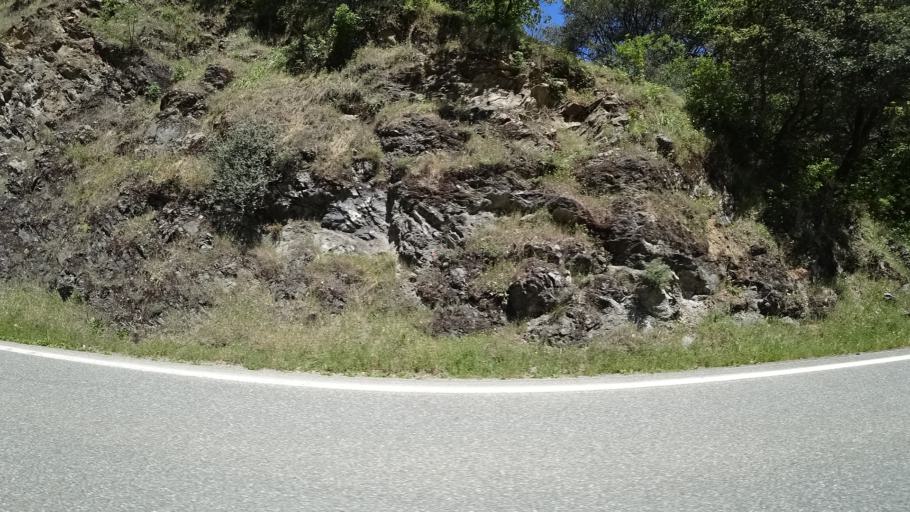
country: US
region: California
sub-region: Trinity County
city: Hayfork
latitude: 40.7708
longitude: -123.3077
